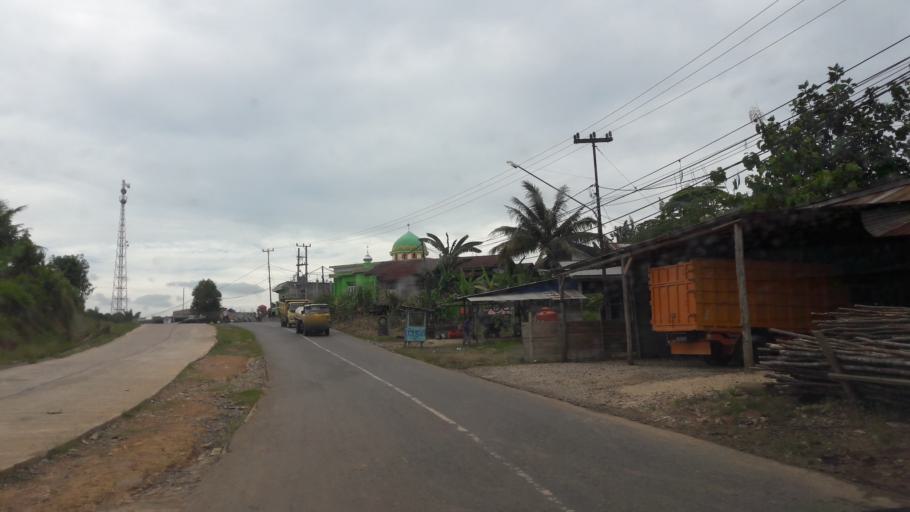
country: ID
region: South Sumatra
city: Gunungmegang Dalam
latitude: -3.2723
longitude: 103.8319
